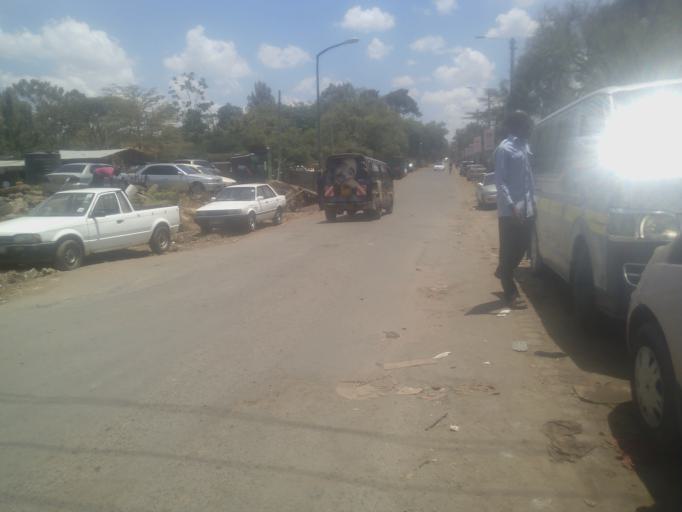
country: KE
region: Nairobi Area
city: Nairobi
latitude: -1.3037
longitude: 36.7812
